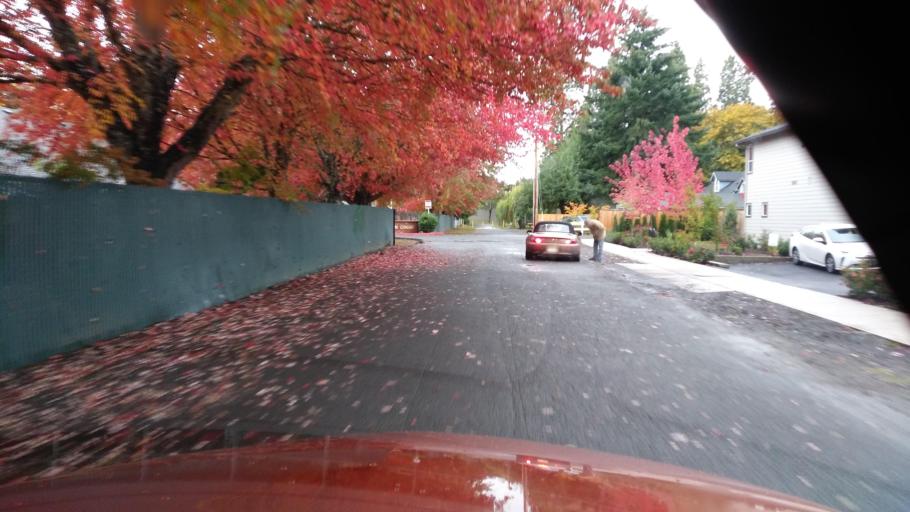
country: US
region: Oregon
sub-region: Washington County
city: Forest Grove
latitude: 45.5221
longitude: -123.0956
